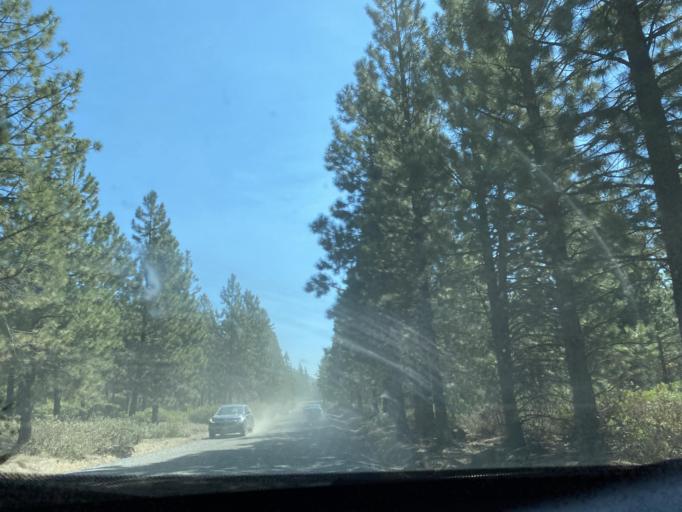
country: US
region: Oregon
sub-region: Deschutes County
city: Sunriver
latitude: 44.0343
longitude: -121.5453
